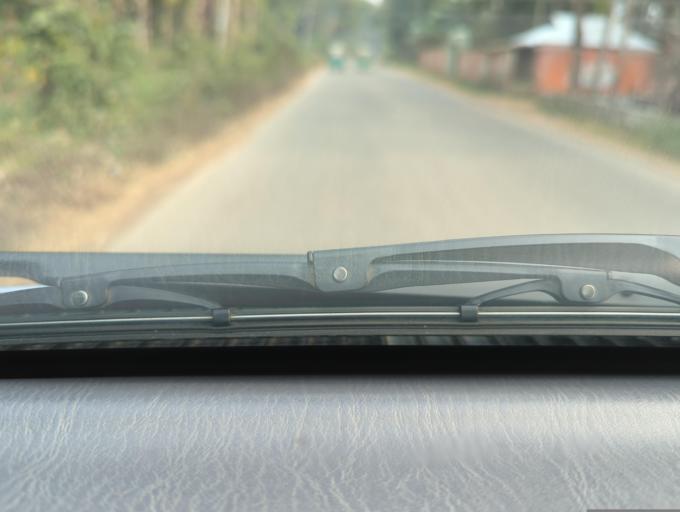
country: BD
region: Sylhet
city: Maulavi Bazar
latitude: 24.4972
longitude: 91.7410
